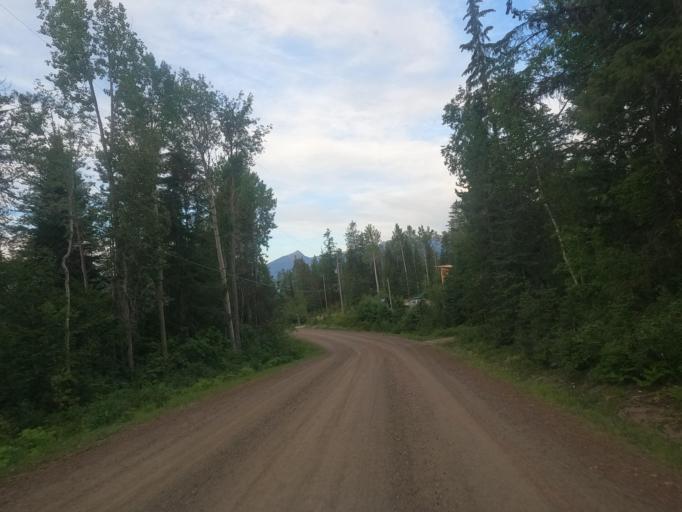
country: CA
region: British Columbia
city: Golden
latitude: 51.4503
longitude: -117.0056
